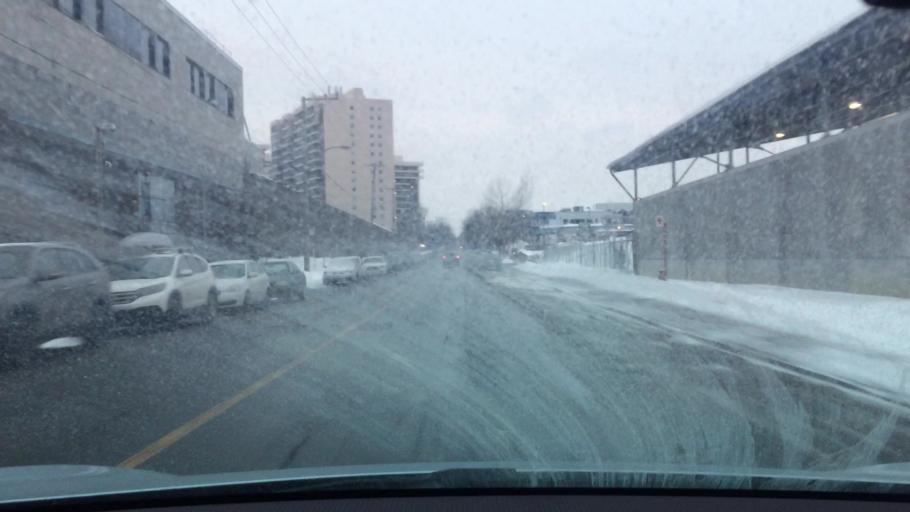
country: CA
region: Quebec
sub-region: Monteregie
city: Longueuil
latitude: 45.5327
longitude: -73.5458
